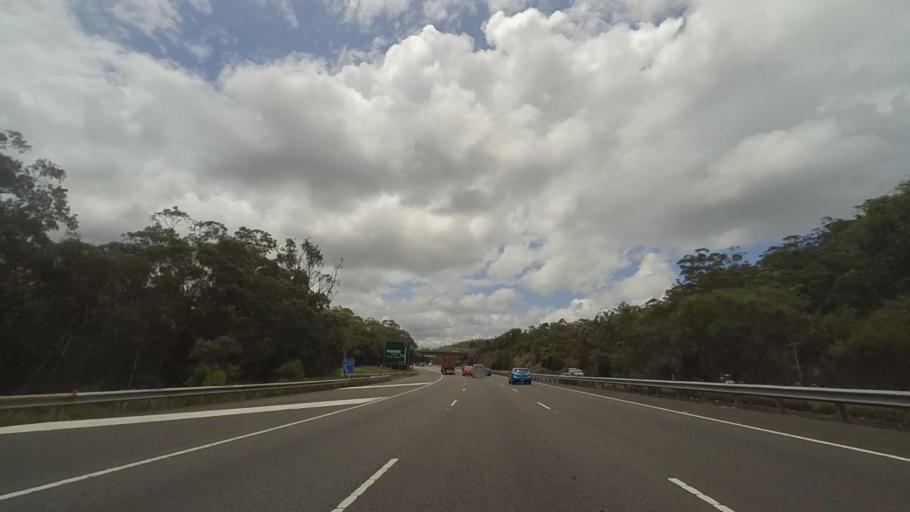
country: AU
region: New South Wales
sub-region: Gosford Shire
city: Point Clare
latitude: -33.4472
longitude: 151.2184
